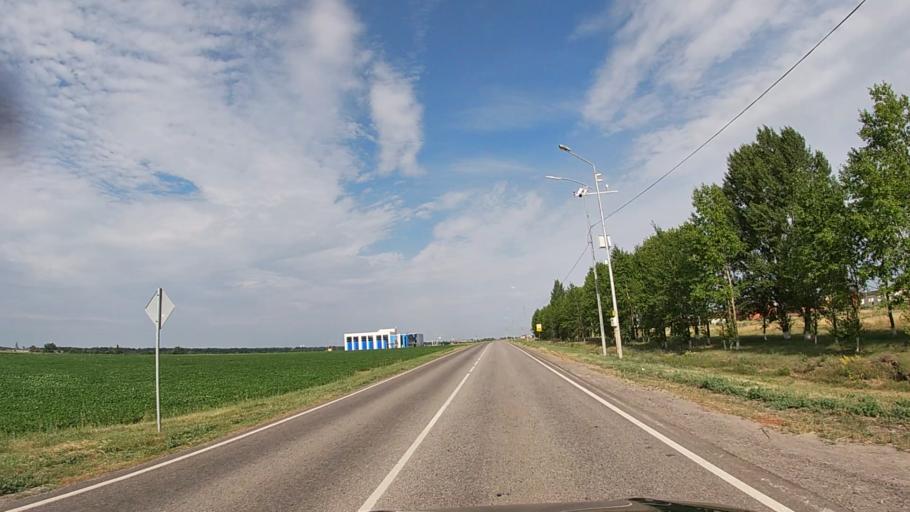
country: RU
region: Belgorod
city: Krasnaya Yaruga
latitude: 50.7962
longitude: 35.6964
